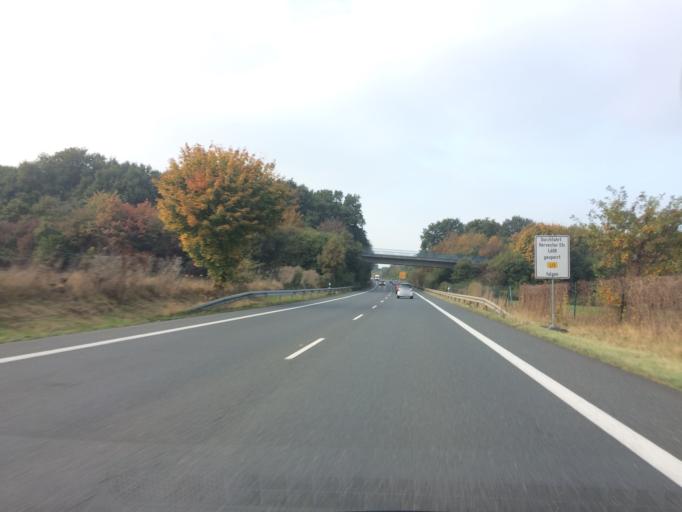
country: DE
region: North Rhine-Westphalia
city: Dorsten
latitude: 51.6807
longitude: 7.0248
